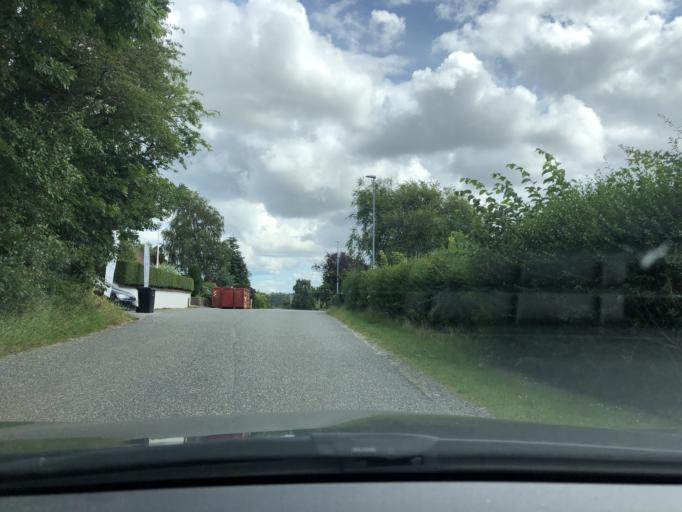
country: DK
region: South Denmark
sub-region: Vejle Kommune
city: Jelling
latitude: 55.6928
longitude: 9.4610
